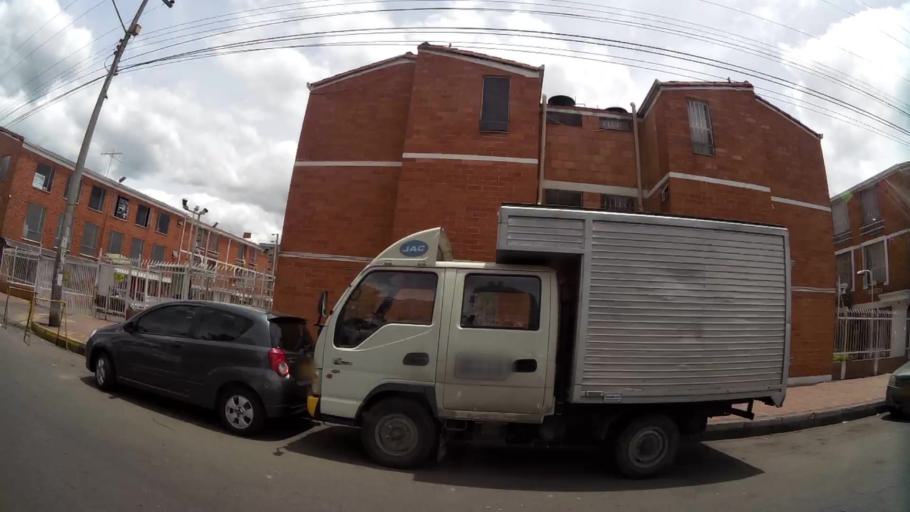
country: CO
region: Bogota D.C.
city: Bogota
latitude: 4.6505
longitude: -74.1506
